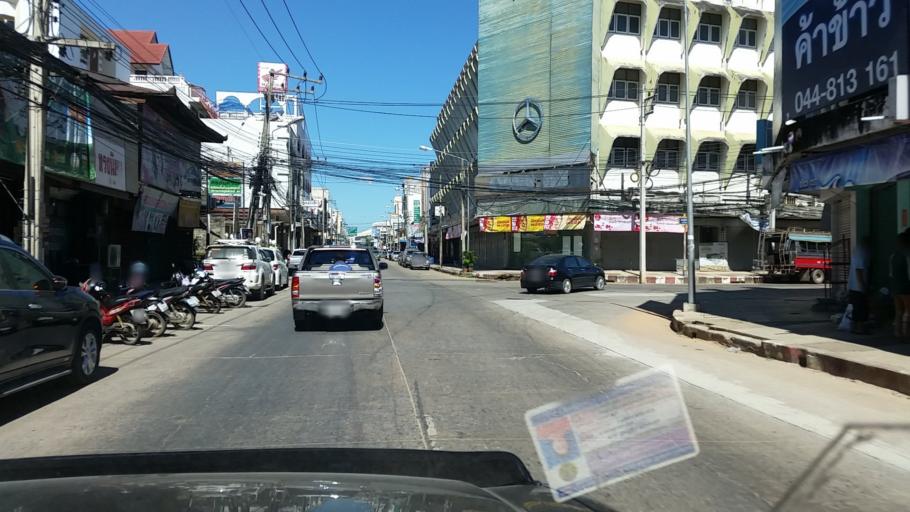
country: TH
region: Chaiyaphum
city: Chaiyaphum
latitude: 15.8098
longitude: 102.0291
